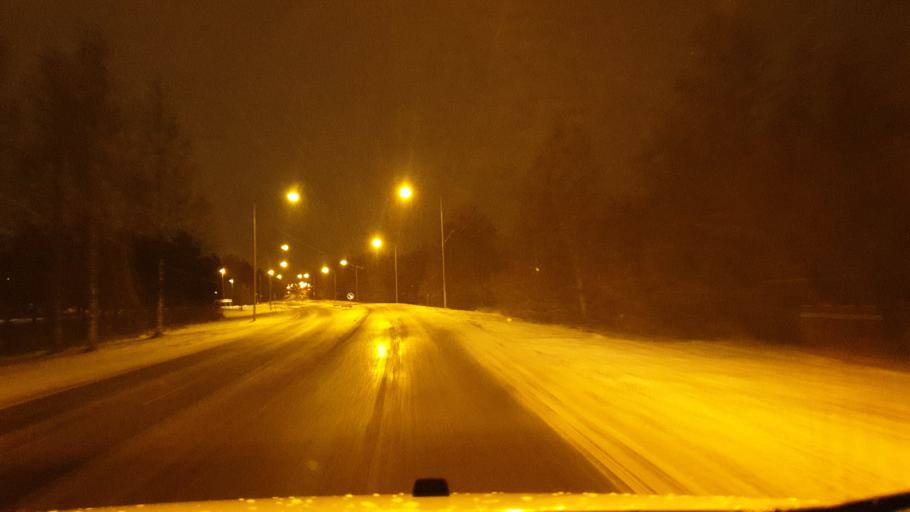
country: FI
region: Northern Ostrobothnia
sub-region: Oulu
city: Oulu
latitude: 64.9831
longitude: 25.4529
